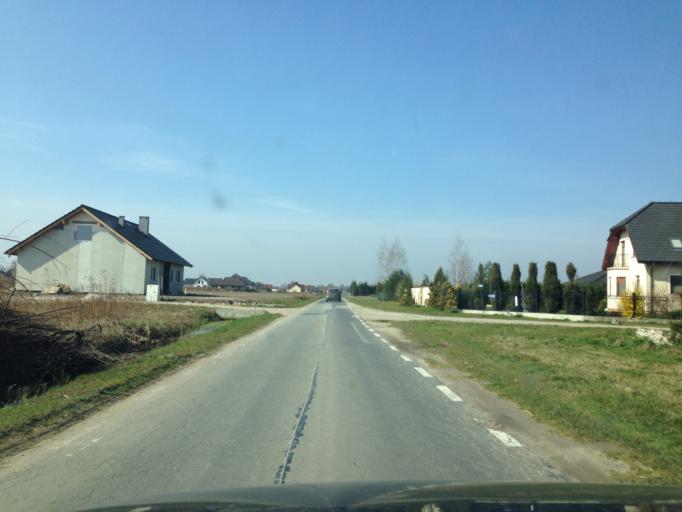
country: PL
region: Lower Silesian Voivodeship
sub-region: Powiat wroclawski
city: Kamieniec Wroclawski
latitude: 51.0984
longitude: 17.2097
